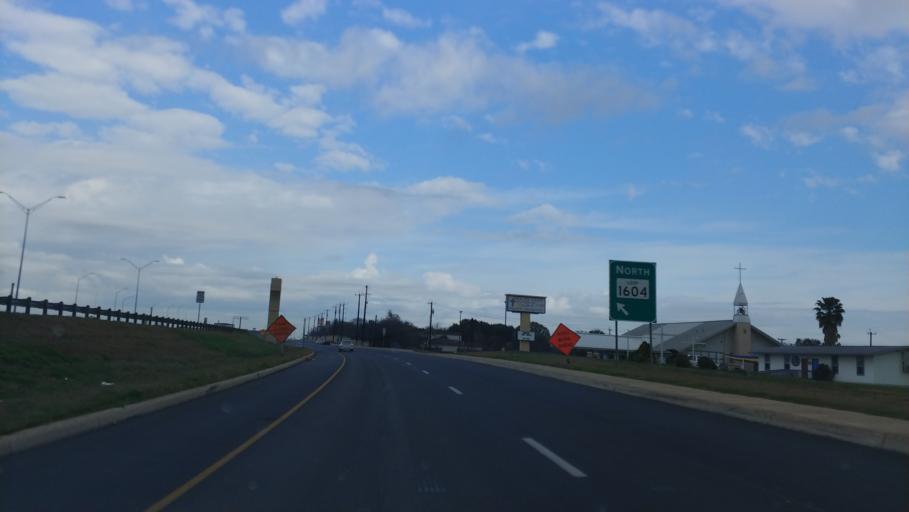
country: US
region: Texas
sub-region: Bexar County
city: Lackland Air Force Base
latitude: 29.3975
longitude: -98.7028
